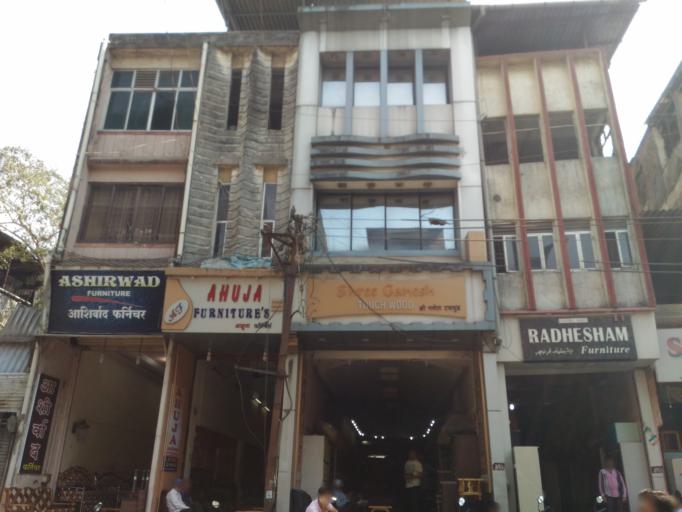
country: IN
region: Maharashtra
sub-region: Thane
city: Ulhasnagar
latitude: 19.2314
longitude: 73.1632
